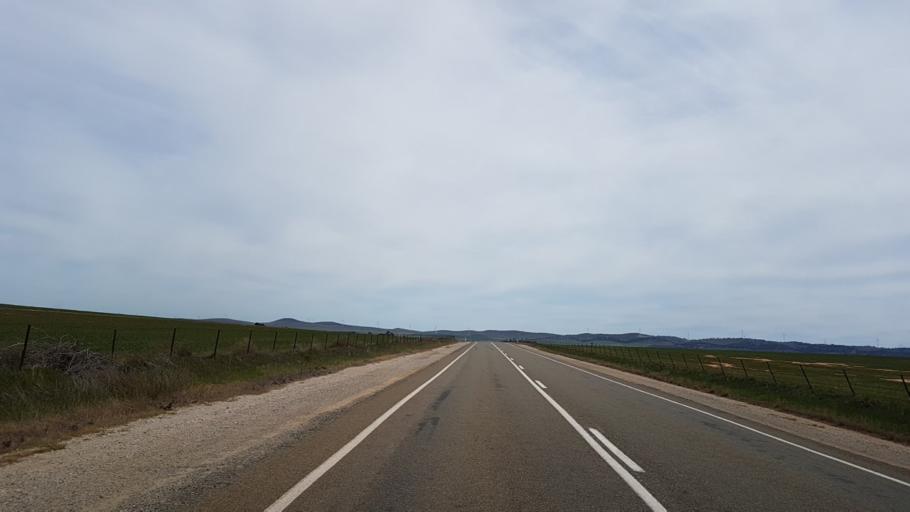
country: AU
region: South Australia
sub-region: Peterborough
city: Peterborough
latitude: -33.0249
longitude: 138.6738
